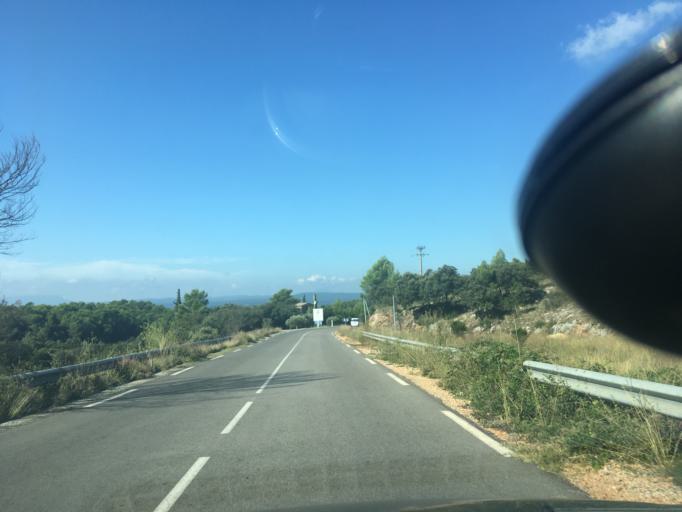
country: FR
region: Provence-Alpes-Cote d'Azur
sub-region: Departement du Var
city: Barjols
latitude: 43.6025
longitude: 6.0572
